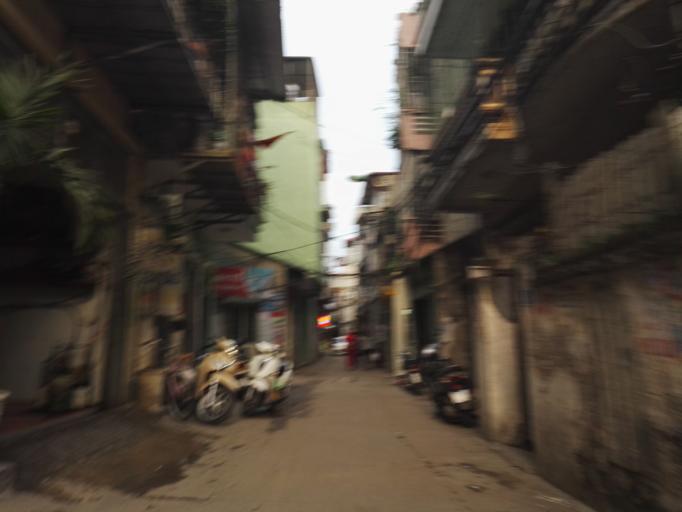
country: VN
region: Ha Noi
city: Hoan Kiem
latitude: 21.0429
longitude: 105.8511
